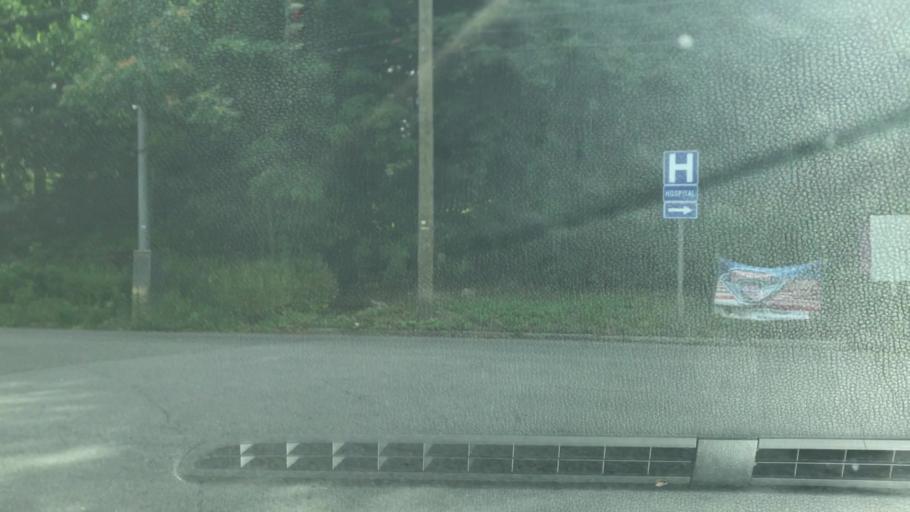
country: US
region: New York
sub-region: Westchester County
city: Tuckahoe
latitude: 40.9516
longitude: -73.7961
